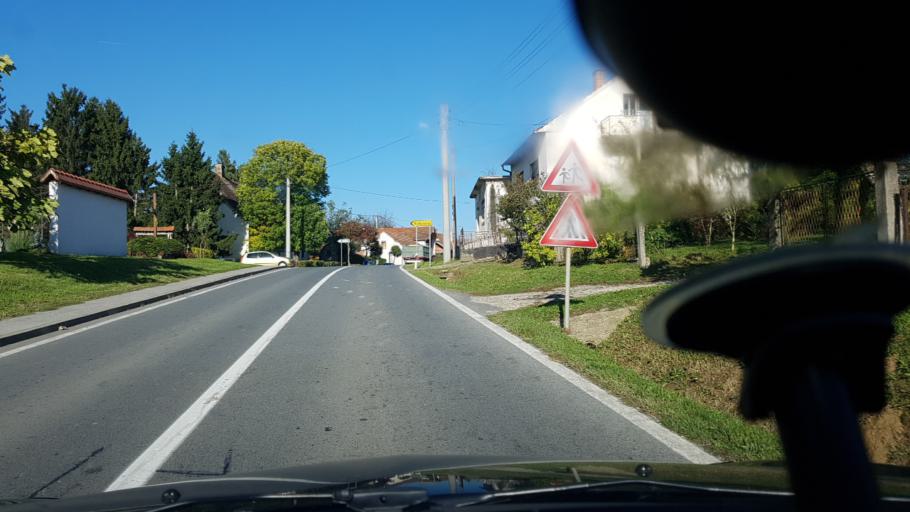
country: HR
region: Bjelovarsko-Bilogorska
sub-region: Grad Cazma
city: Cazma
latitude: 45.7836
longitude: 16.6465
